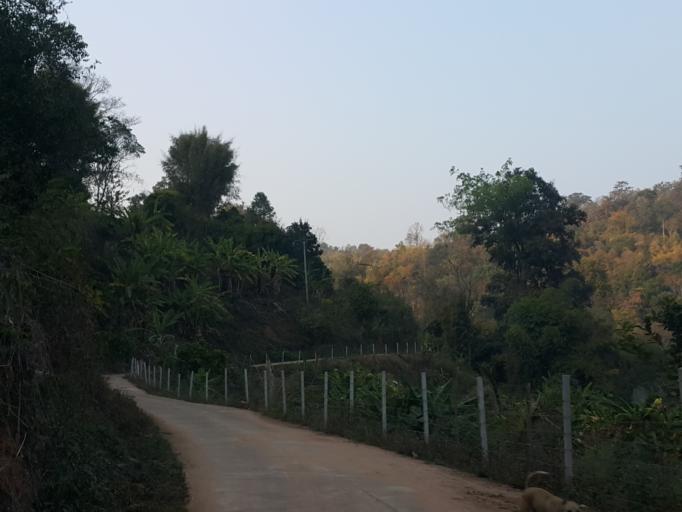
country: TH
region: Chiang Mai
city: Mae Taeng
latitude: 19.0673
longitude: 98.7739
